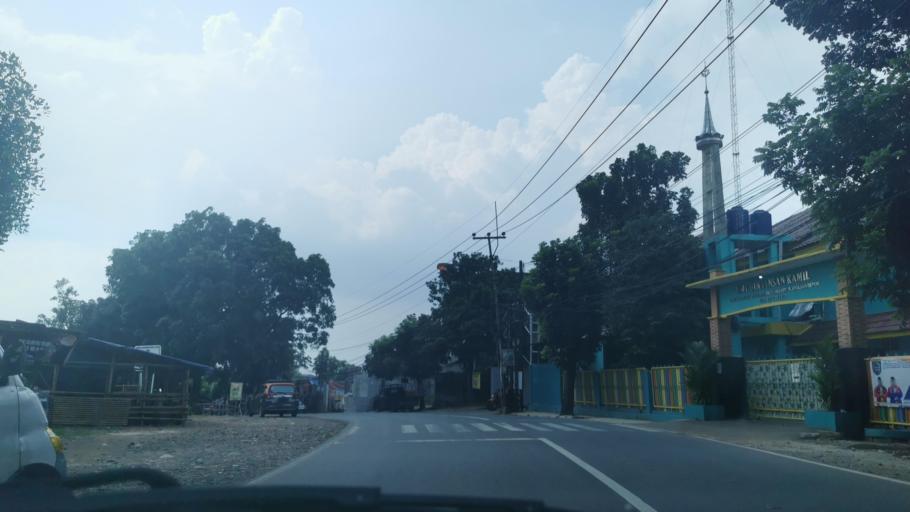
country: ID
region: West Java
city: Depok
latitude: -6.4107
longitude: 106.8315
